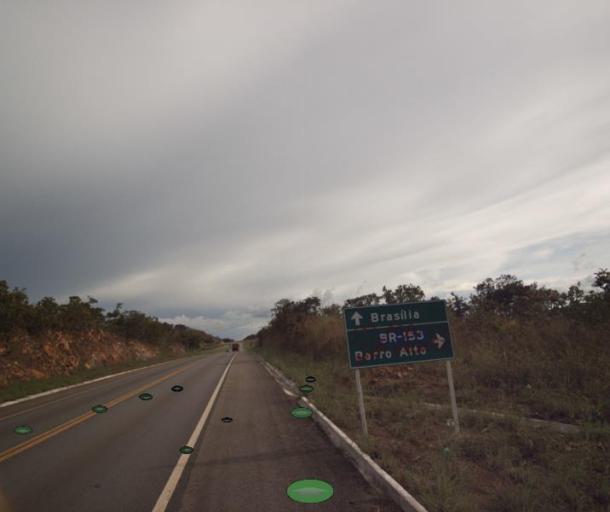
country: BR
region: Goias
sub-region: Barro Alto
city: Barro Alto
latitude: -15.0989
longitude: -48.7478
